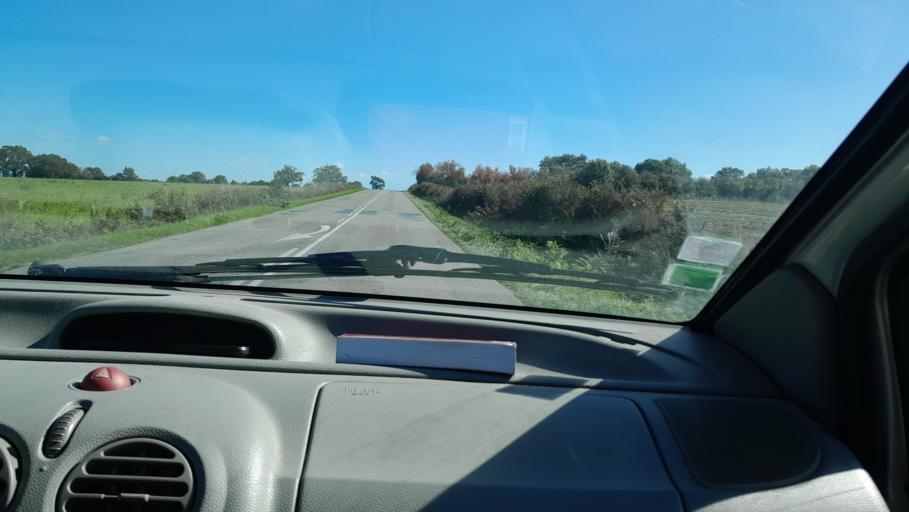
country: FR
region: Pays de la Loire
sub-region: Departement de la Mayenne
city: Quelaines-Saint-Gault
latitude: 47.9346
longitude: -0.8503
